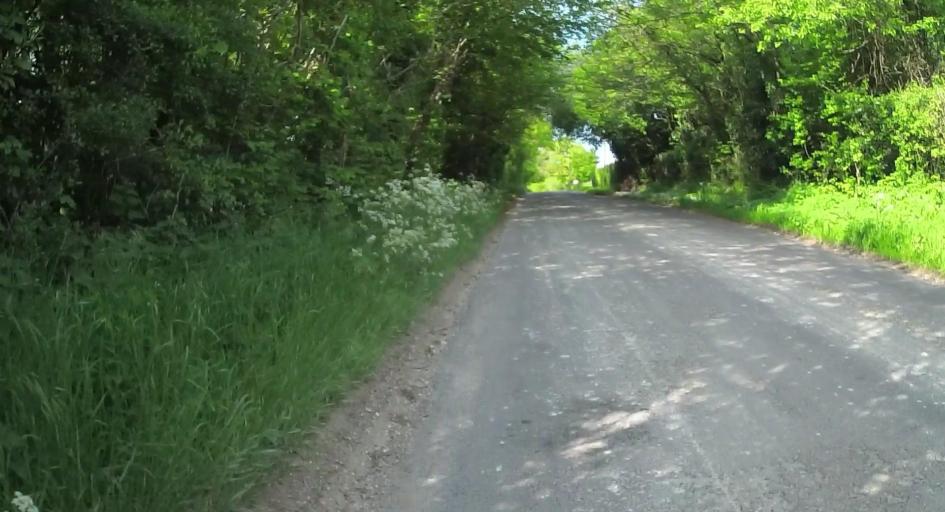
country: GB
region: England
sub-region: Hampshire
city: Four Marks
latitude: 51.1419
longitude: -1.0637
